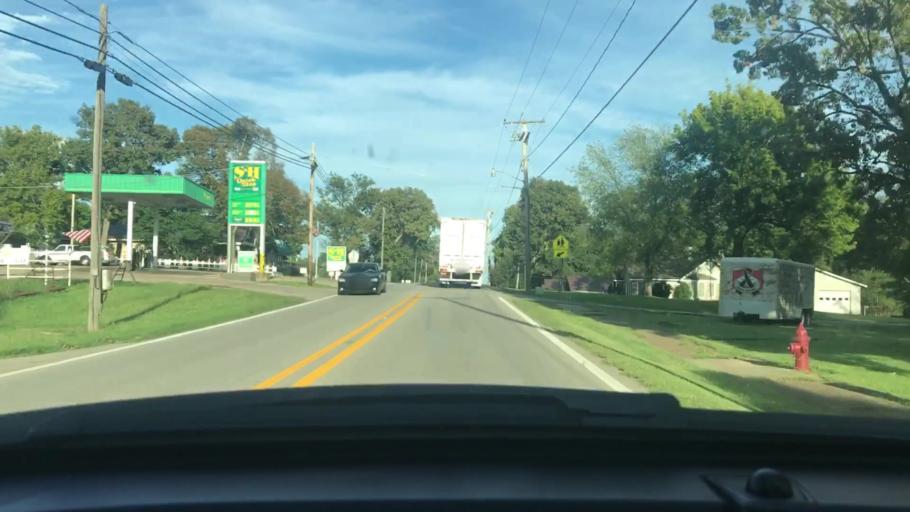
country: US
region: Arkansas
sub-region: Randolph County
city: Pocahontas
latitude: 36.2038
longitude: -91.1826
